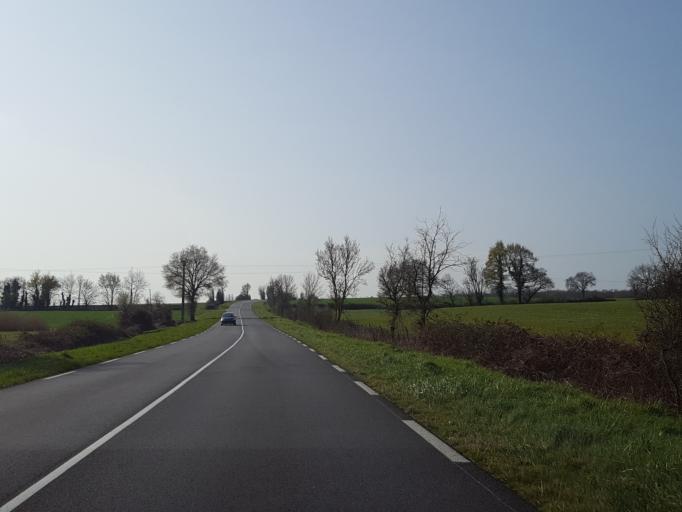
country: FR
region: Pays de la Loire
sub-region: Departement de la Vendee
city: Rocheserviere
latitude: 46.9124
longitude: -1.5053
